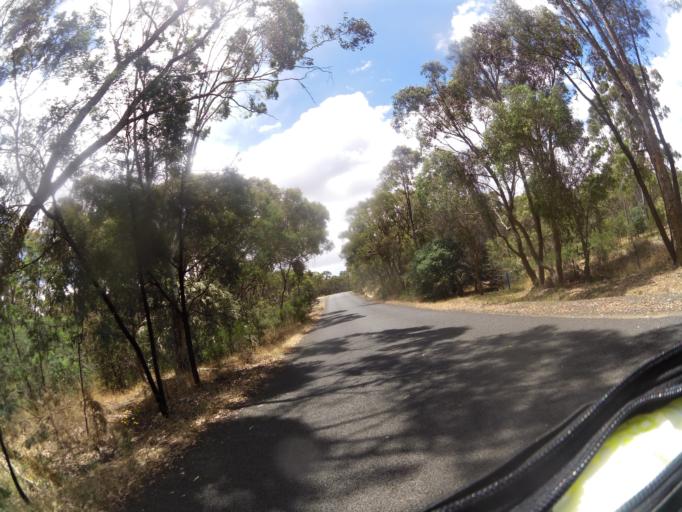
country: AU
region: Victoria
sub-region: Mount Alexander
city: Castlemaine
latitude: -37.0231
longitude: 144.2422
